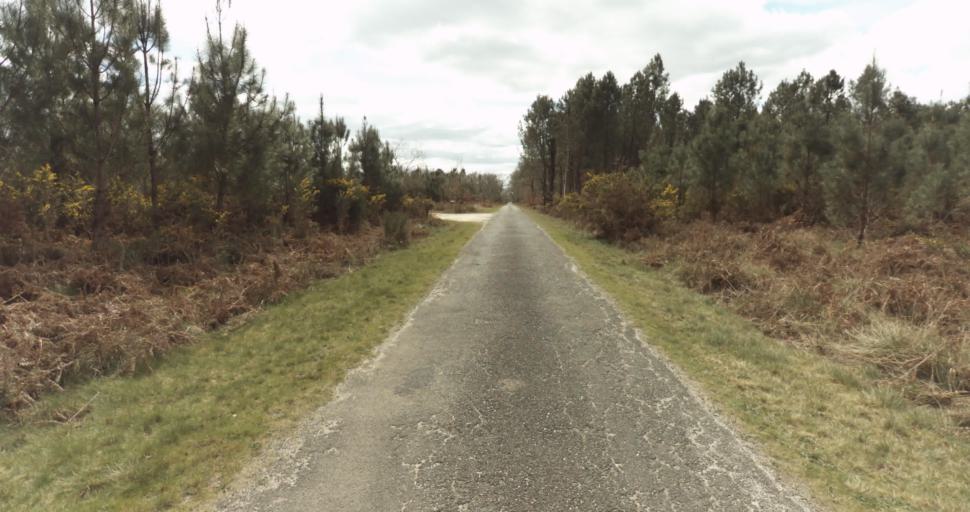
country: FR
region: Aquitaine
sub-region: Departement des Landes
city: Roquefort
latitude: 44.0982
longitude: -0.4392
